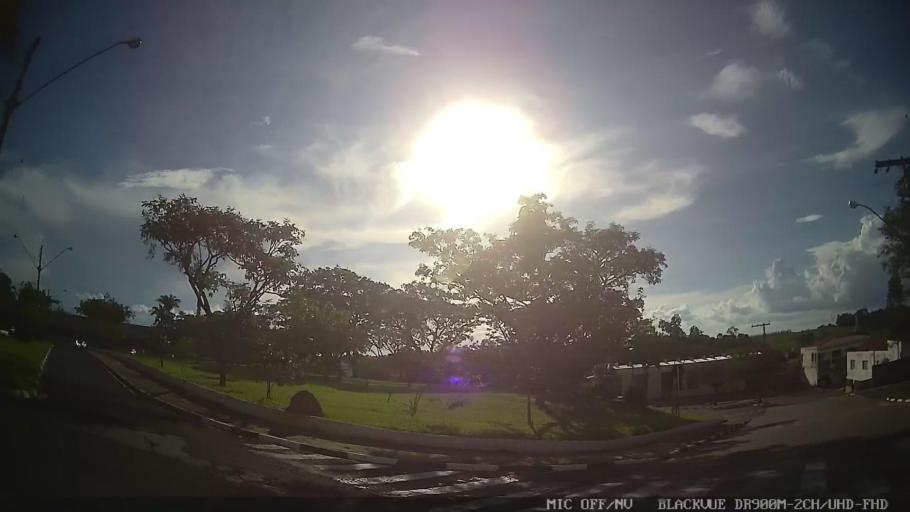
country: BR
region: Sao Paulo
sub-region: Tiete
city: Tiete
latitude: -23.1103
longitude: -47.7175
